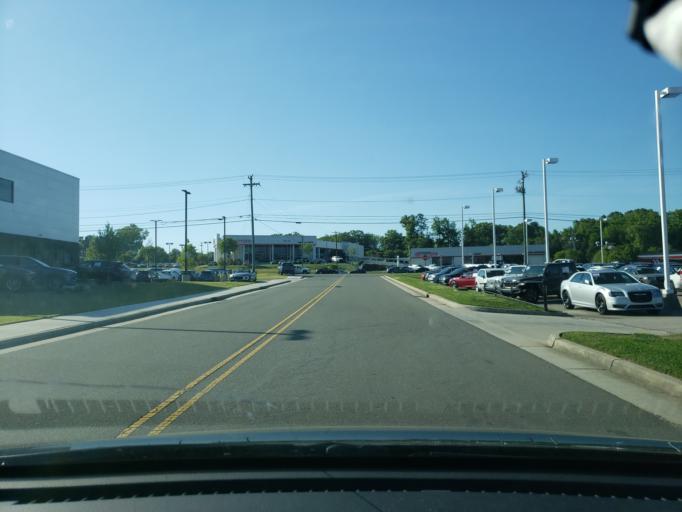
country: US
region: North Carolina
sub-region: Durham County
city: Durham
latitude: 35.9618
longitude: -78.9743
